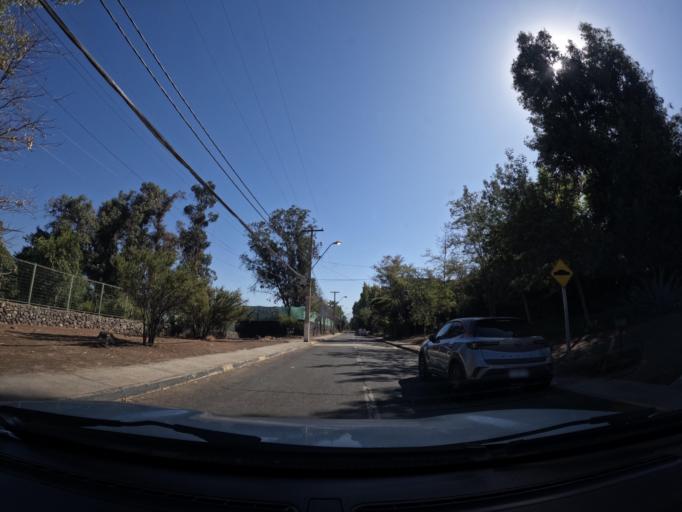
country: CL
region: Santiago Metropolitan
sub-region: Provincia de Santiago
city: Villa Presidente Frei, Nunoa, Santiago, Chile
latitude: -33.4970
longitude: -70.5361
